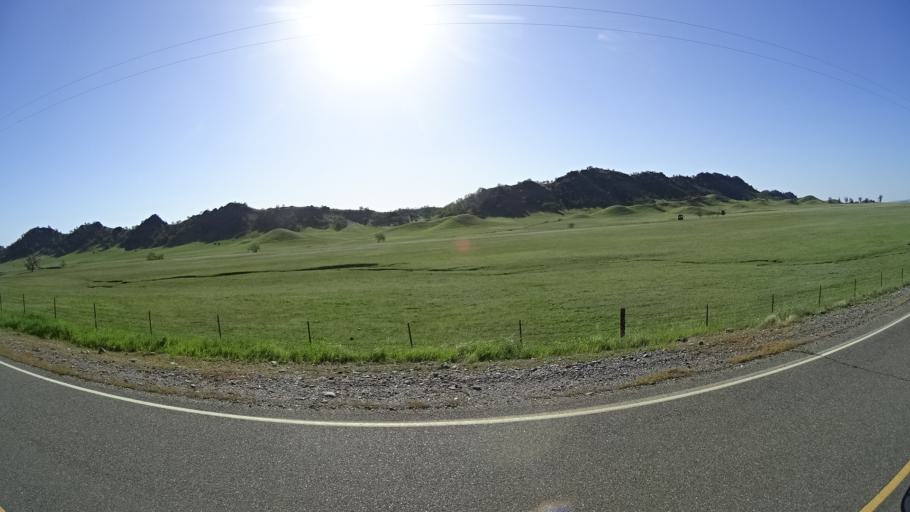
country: US
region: California
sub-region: Tehama County
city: Rancho Tehama Reserve
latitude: 39.7410
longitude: -122.5460
